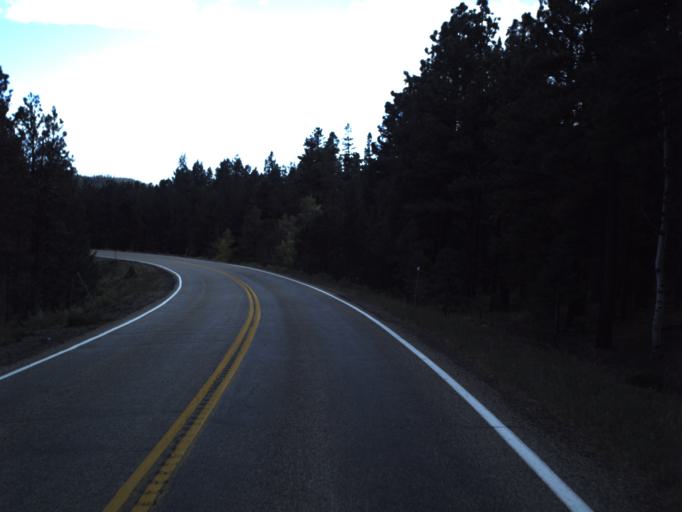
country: US
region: Utah
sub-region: Garfield County
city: Panguitch
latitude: 37.4941
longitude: -112.6201
